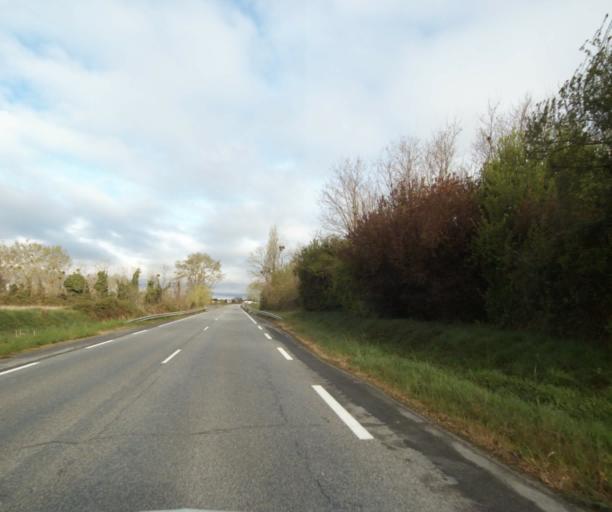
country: FR
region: Midi-Pyrenees
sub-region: Departement de l'Ariege
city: Saverdun
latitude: 43.2422
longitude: 1.5811
